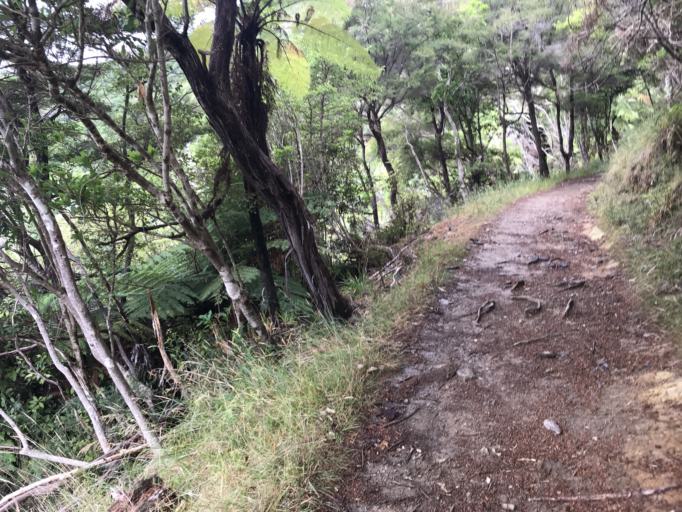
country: NZ
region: Marlborough
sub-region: Marlborough District
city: Picton
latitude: -41.2310
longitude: 173.9583
